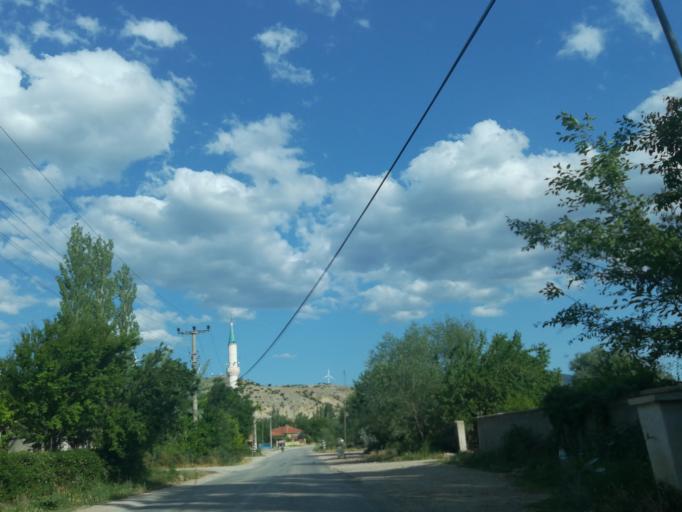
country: TR
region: Afyonkarahisar
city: Dinar
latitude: 38.0830
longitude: 30.1653
